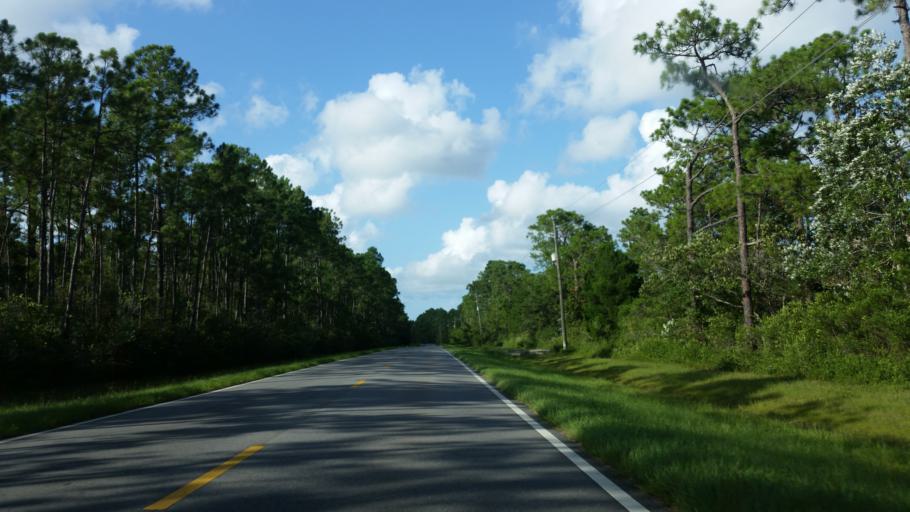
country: US
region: Florida
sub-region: Santa Rosa County
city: Bagdad
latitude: 30.5377
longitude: -87.0508
